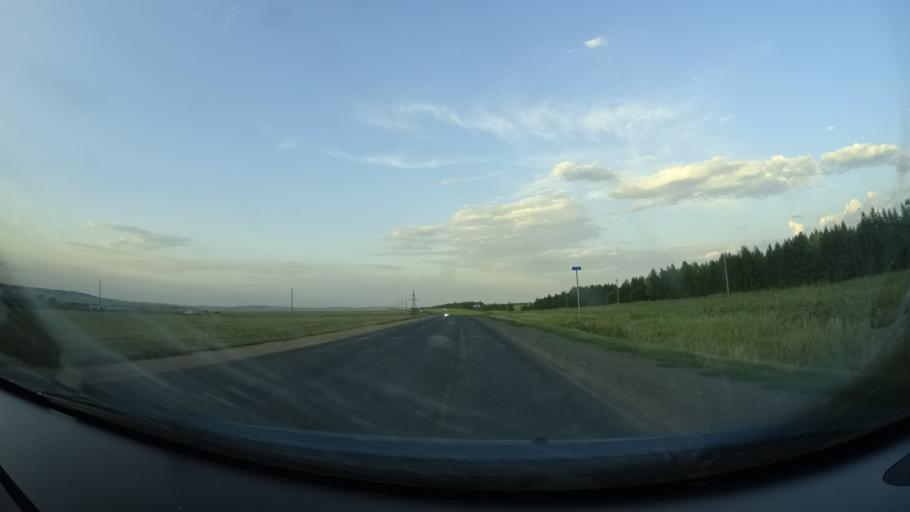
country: RU
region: Orenburg
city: Severnoye
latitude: 54.0888
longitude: 52.4497
